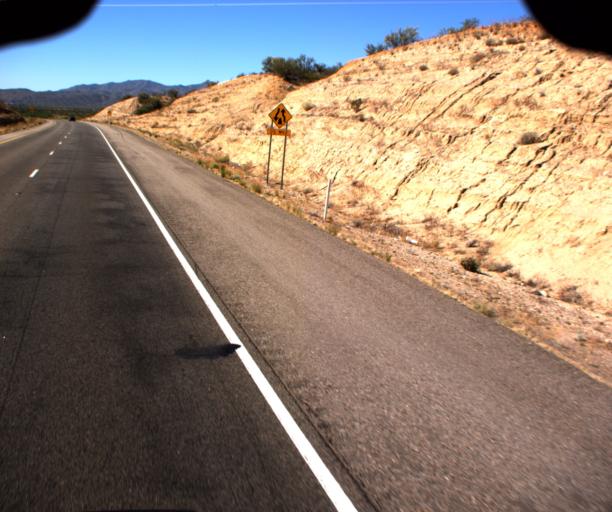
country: US
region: Arizona
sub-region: Yavapai County
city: Bagdad
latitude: 34.7503
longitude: -113.6165
